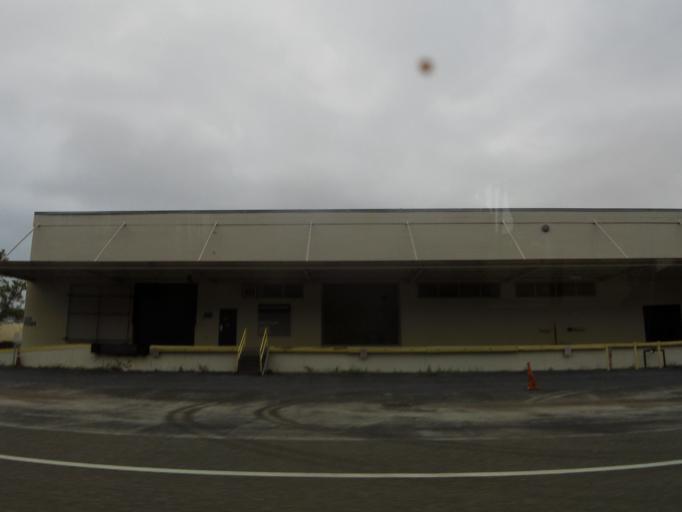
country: US
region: Florida
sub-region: Duval County
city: Baldwin
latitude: 30.2233
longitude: -81.8896
